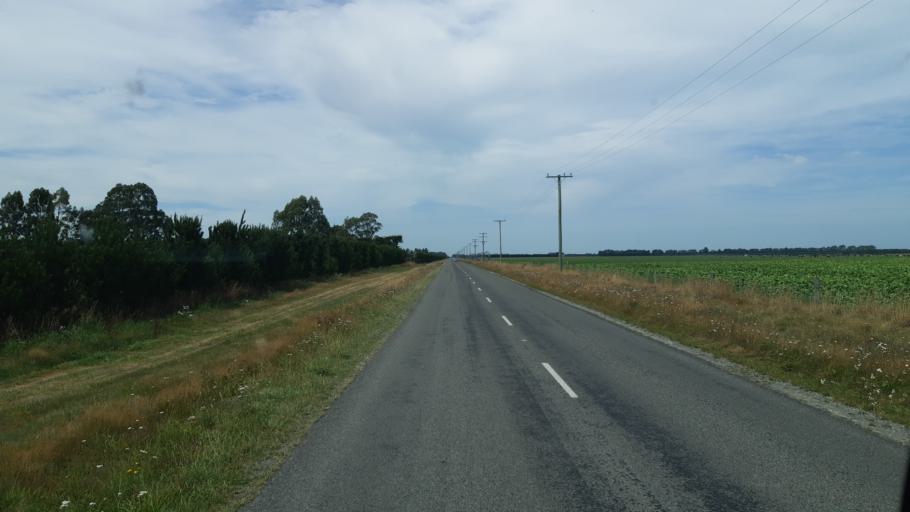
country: NZ
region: Canterbury
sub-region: Ashburton District
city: Tinwald
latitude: -43.9253
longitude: 171.5657
